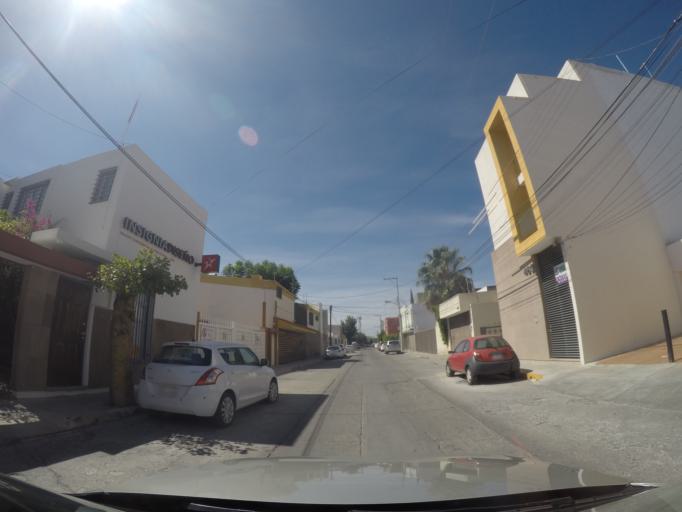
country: MX
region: San Luis Potosi
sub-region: San Luis Potosi
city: San Luis Potosi
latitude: 22.1511
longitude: -101.0076
